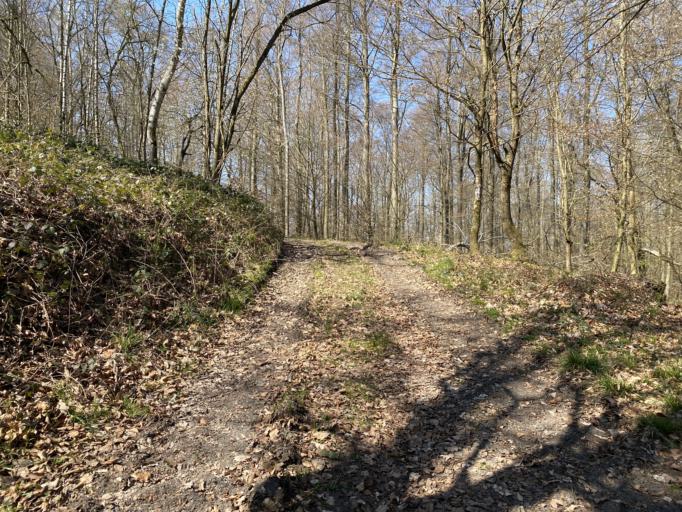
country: DE
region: Hesse
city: Budingen
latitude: 50.2385
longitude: 9.0727
